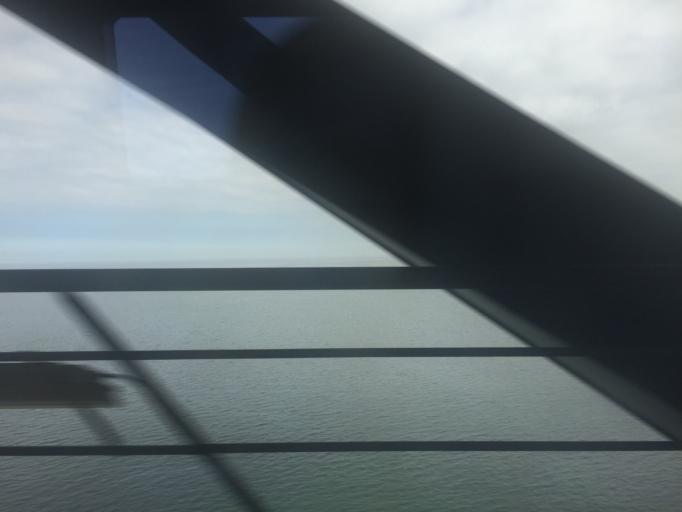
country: SE
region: Skane
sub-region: Malmo
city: Bunkeflostrand
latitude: 55.5645
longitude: 12.8952
